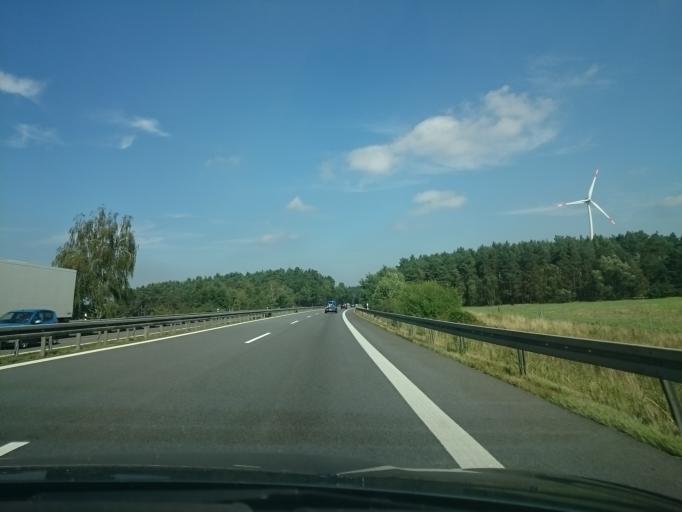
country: DE
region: Brandenburg
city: Calau
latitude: 51.7428
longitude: 13.8619
